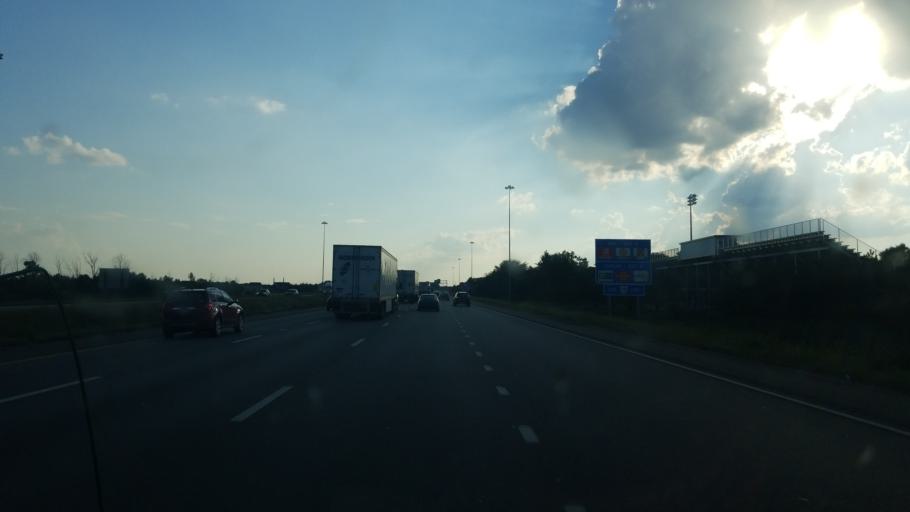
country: US
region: Ohio
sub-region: Wood County
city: Perrysburg
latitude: 41.5464
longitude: -83.6074
